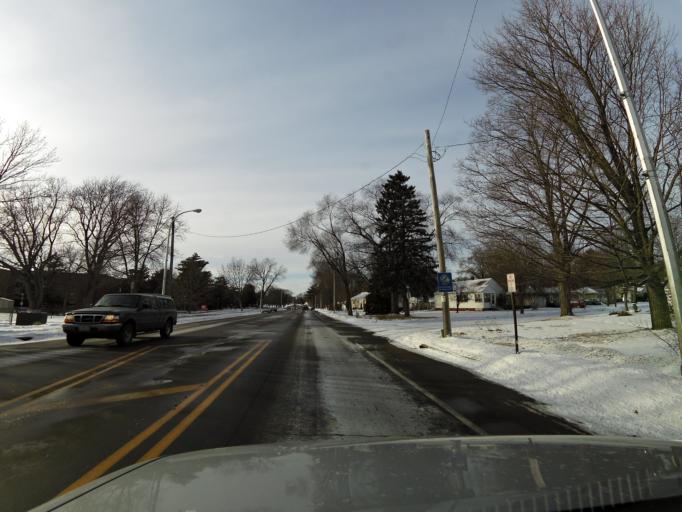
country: US
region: Wisconsin
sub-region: Pierce County
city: River Falls
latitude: 44.8525
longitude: -92.6131
